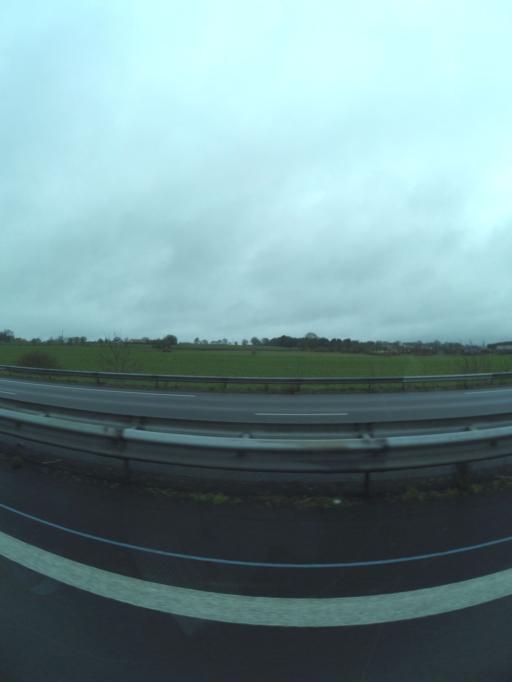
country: FR
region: Pays de la Loire
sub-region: Departement de la Sarthe
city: Louplande
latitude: 47.9490
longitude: -0.0102
